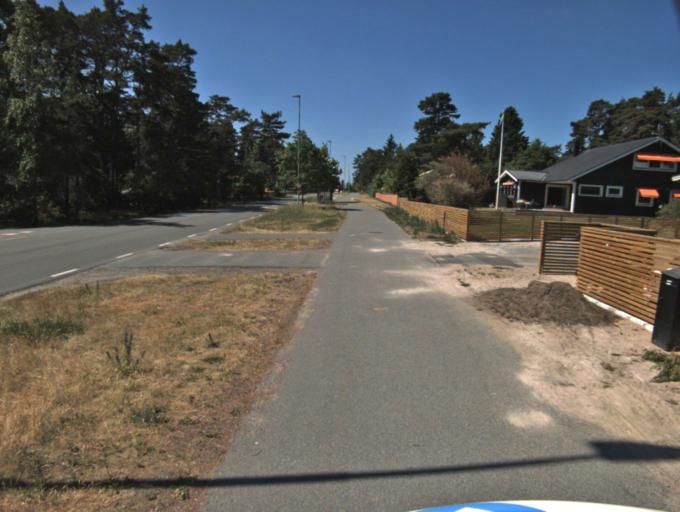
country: SE
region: Skane
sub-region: Kristianstads Kommun
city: Ahus
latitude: 55.9376
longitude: 14.3123
